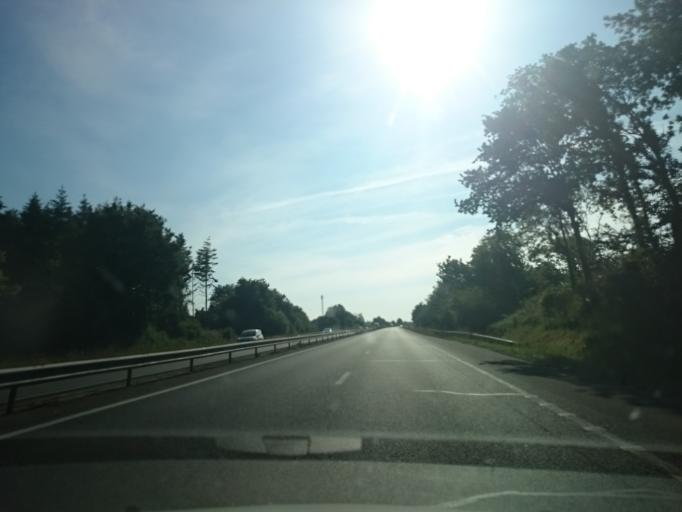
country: FR
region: Brittany
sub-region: Departement du Finistere
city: Pont-Aven
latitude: 47.8863
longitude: -3.7214
